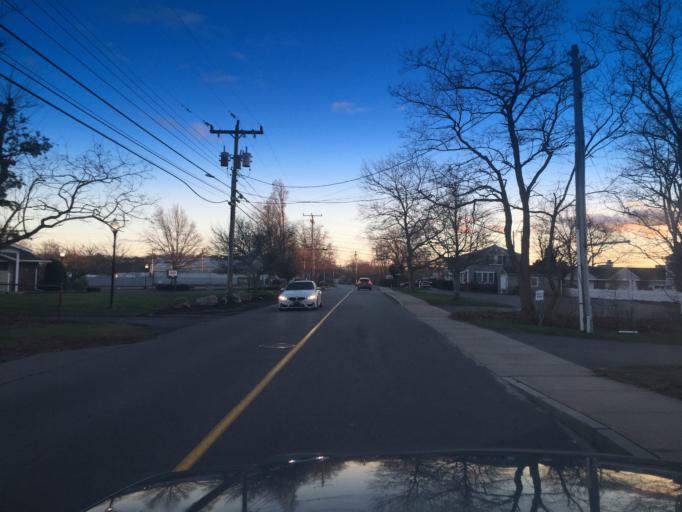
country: US
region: Massachusetts
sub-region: Barnstable County
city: Teaticket
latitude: 41.5589
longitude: -70.5975
